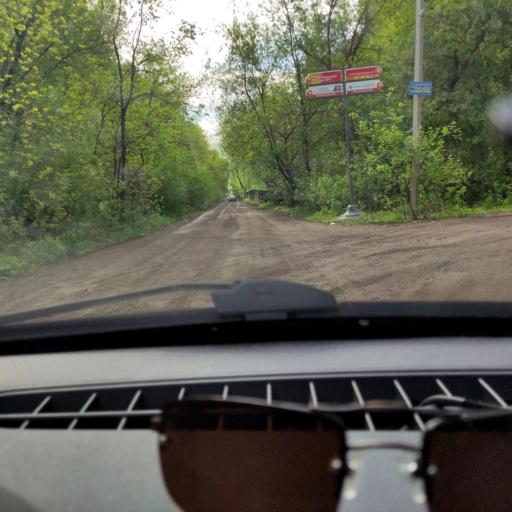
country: RU
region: Bashkortostan
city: Ufa
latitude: 54.6992
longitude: 55.9332
